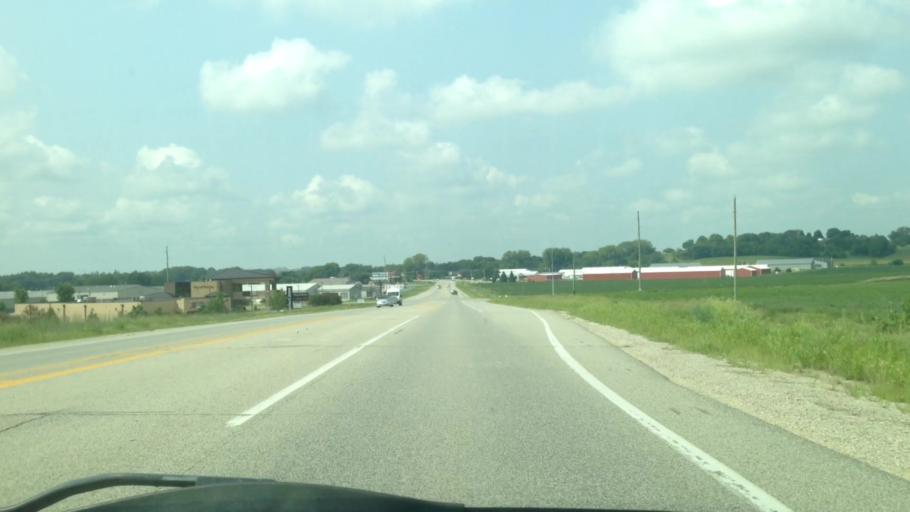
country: US
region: Iowa
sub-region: Linn County
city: Fairfax
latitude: 41.9323
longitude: -91.7718
